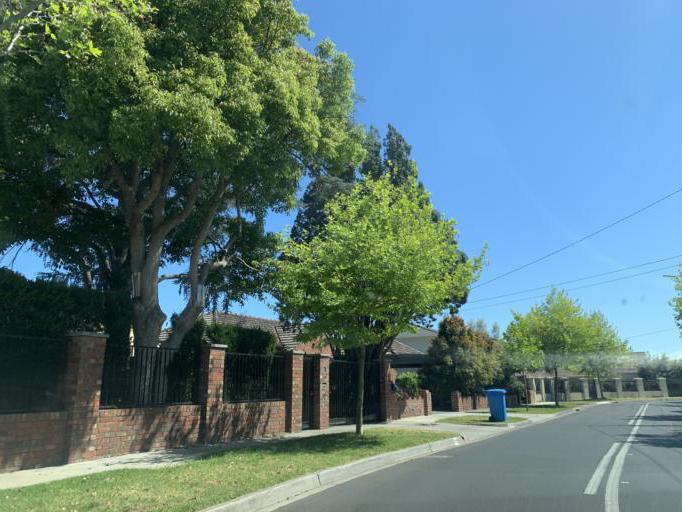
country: AU
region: Victoria
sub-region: Bayside
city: Hampton
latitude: -37.9266
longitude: 145.0084
